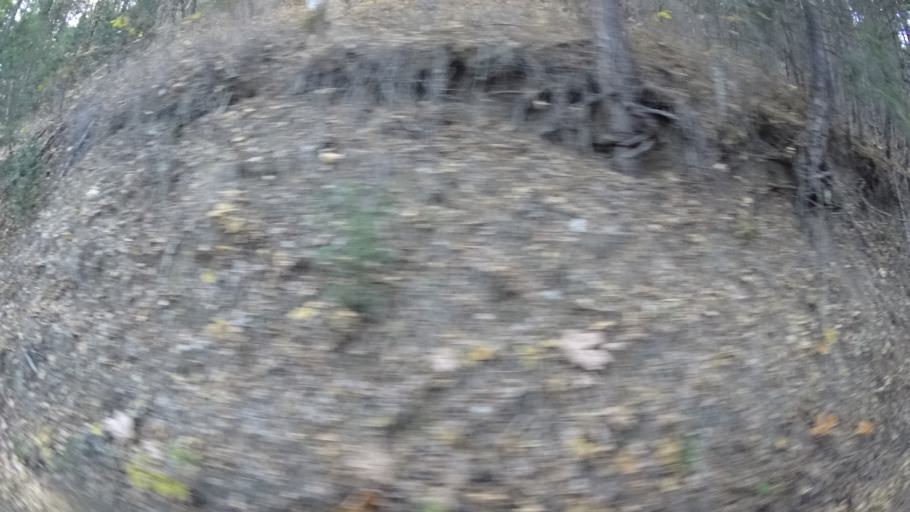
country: US
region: California
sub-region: Siskiyou County
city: Yreka
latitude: 41.8399
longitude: -122.8751
